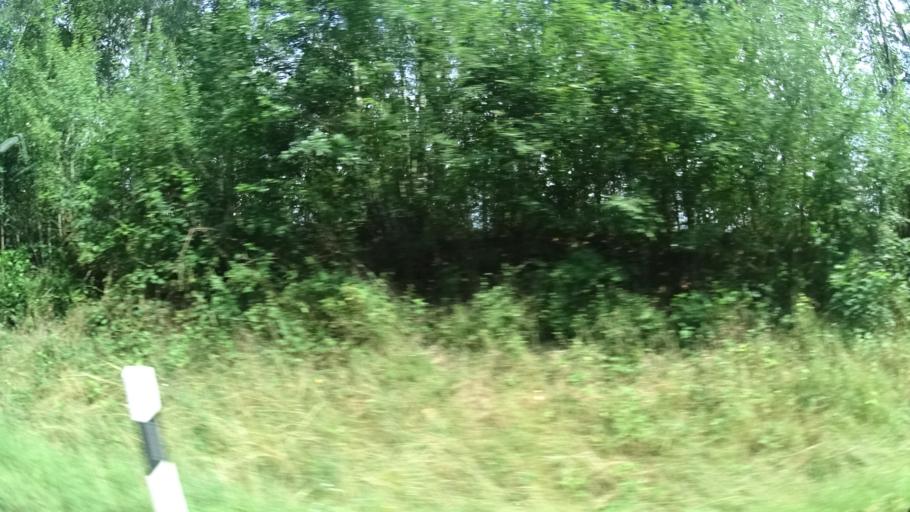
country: DE
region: Hesse
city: Grebenau
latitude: 50.6991
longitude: 9.4468
